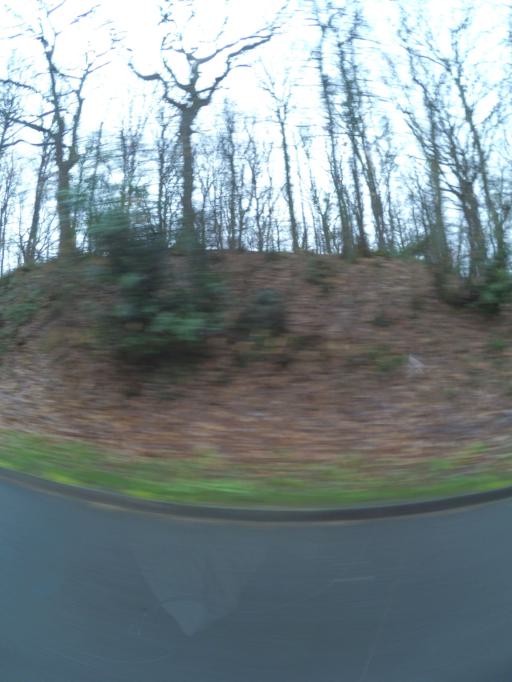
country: FR
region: Pays de la Loire
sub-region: Departement de la Sarthe
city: Saint-Saturnin
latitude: 48.0566
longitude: 0.1540
